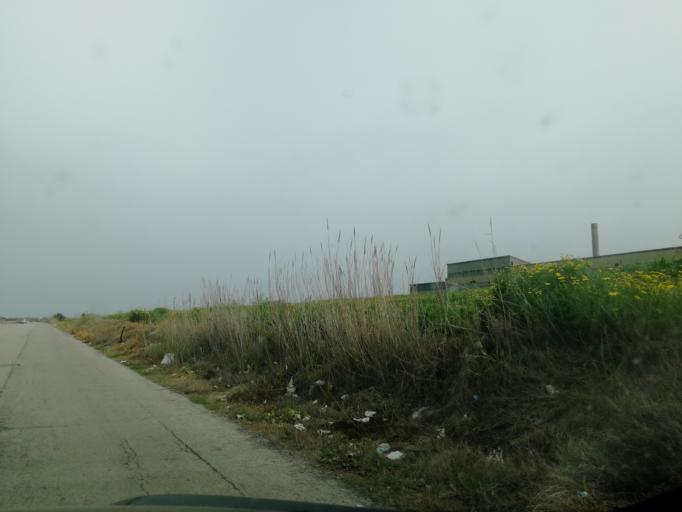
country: IT
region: Apulia
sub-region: Provincia di Barletta - Andria - Trani
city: Barletta
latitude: 41.3186
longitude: 16.3035
